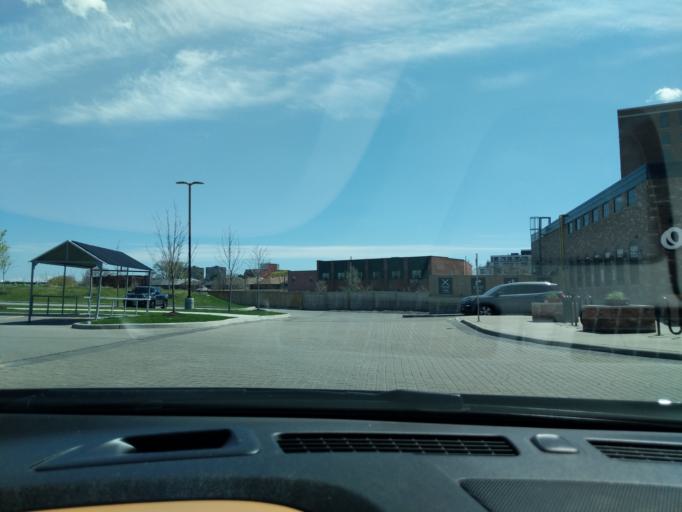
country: CA
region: Ontario
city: Toronto
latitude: 43.6679
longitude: -79.4630
